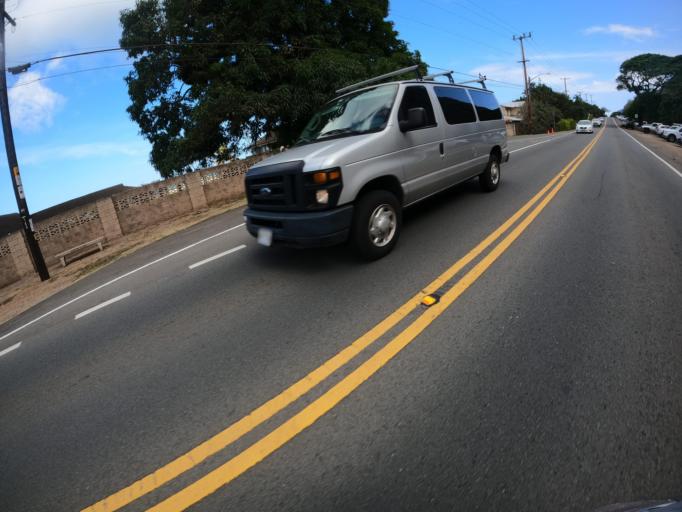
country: US
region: Hawaii
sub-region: Honolulu County
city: Waimanalo Beach
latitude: 21.3245
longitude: -157.6816
